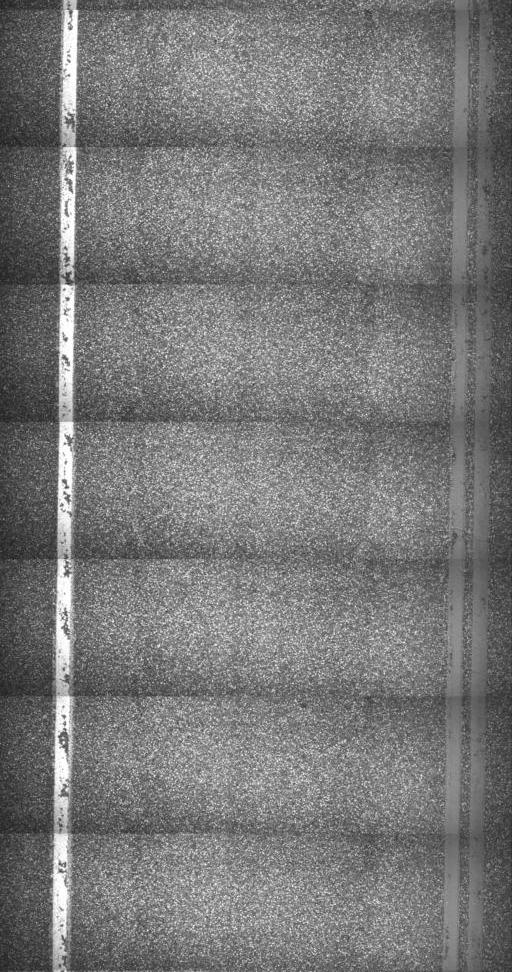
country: US
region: Vermont
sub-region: Franklin County
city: Swanton
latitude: 45.0063
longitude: -73.0814
